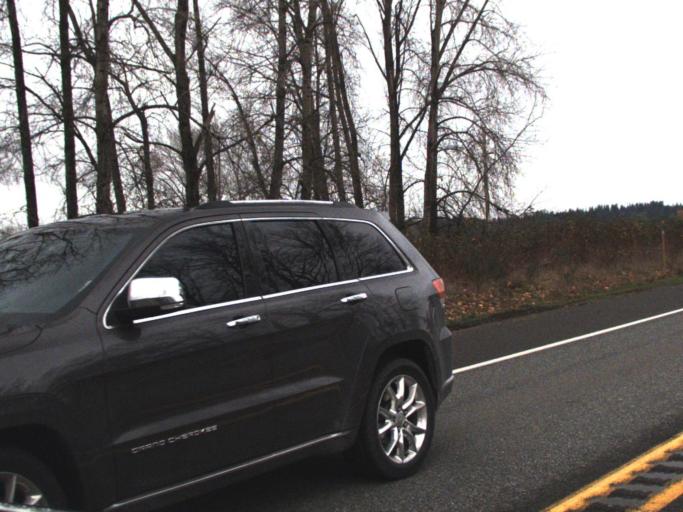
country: US
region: Washington
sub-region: Snohomish County
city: Snohomish
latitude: 47.9093
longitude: -122.1088
